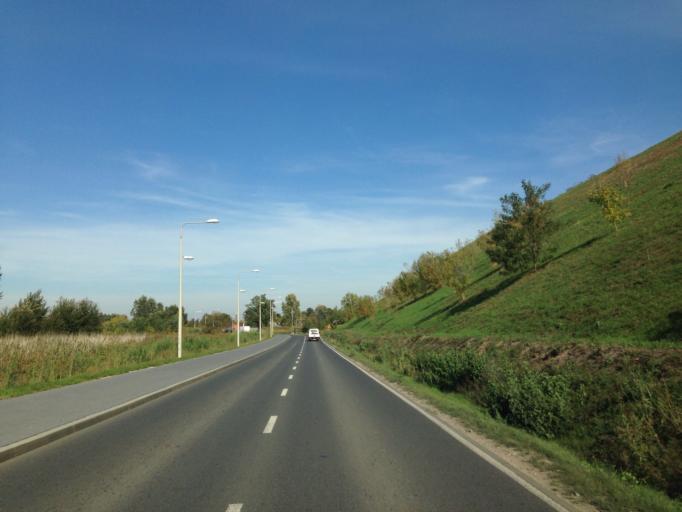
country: PL
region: Masovian Voivodeship
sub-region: Powiat pruszkowski
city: Pruszkow
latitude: 52.1772
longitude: 20.7726
